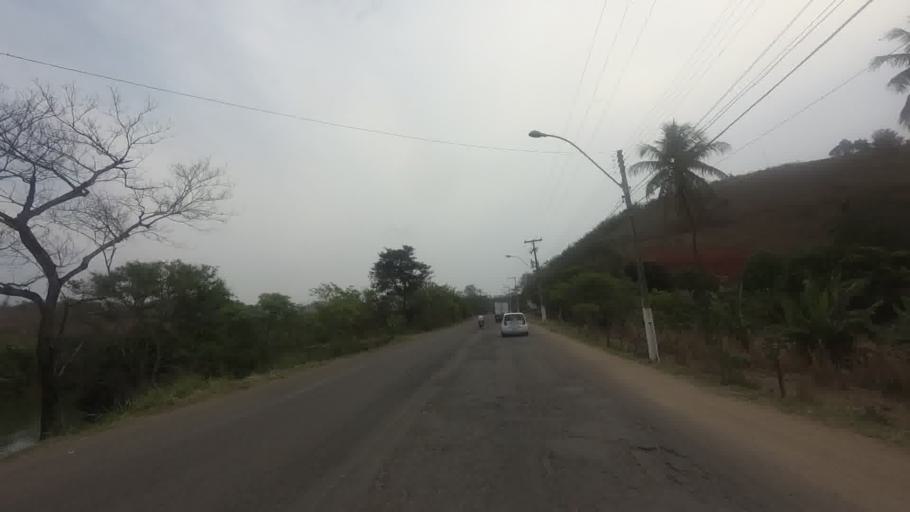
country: BR
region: Rio de Janeiro
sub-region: Santo Antonio De Padua
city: Santo Antonio de Padua
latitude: -21.5452
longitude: -42.1682
